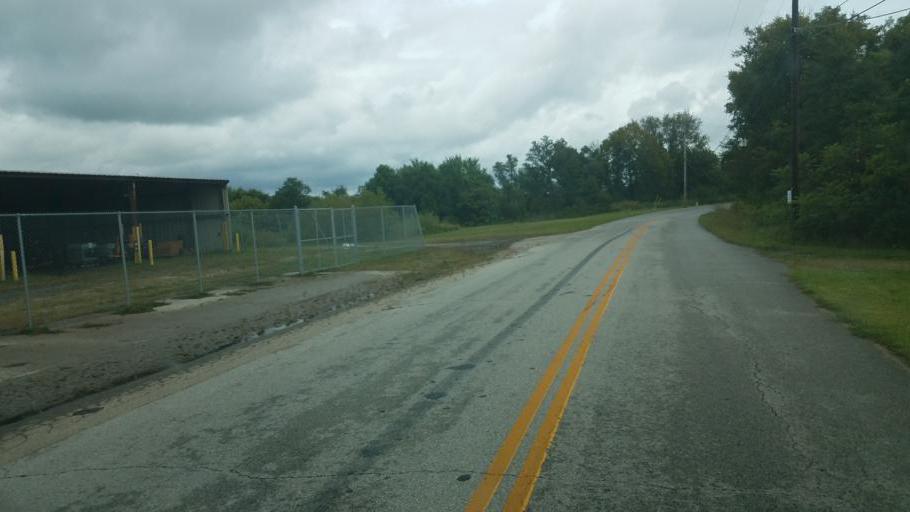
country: US
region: Ohio
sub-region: Scioto County
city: Wheelersburg
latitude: 38.7122
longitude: -82.8691
